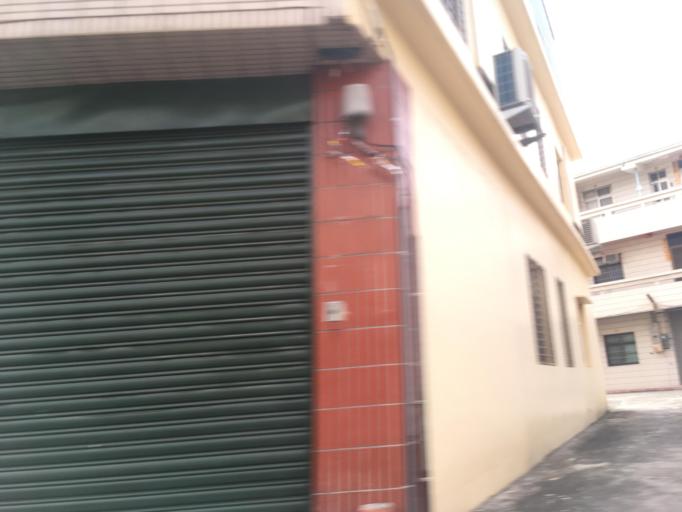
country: TW
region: Taiwan
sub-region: Yunlin
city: Douliu
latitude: 23.6898
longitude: 120.4674
